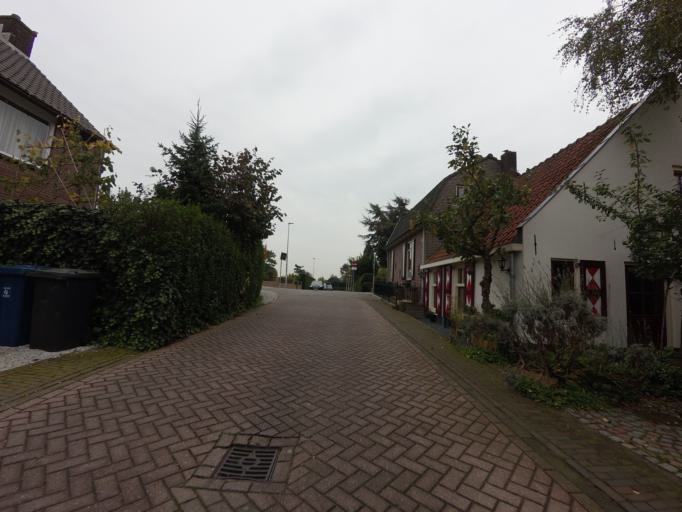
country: NL
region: Utrecht
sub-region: Gemeente Vianen
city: Vianen
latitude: 51.9801
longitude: 5.1182
